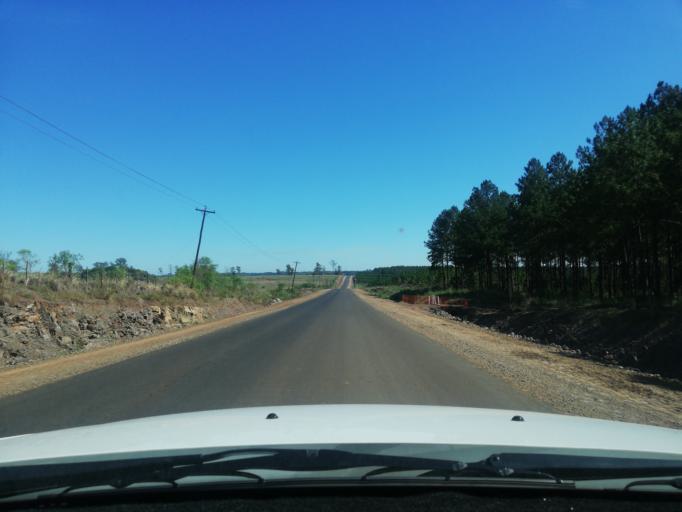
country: AR
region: Misiones
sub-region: Departamento de Candelaria
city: Candelaria
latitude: -27.5092
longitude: -55.7363
